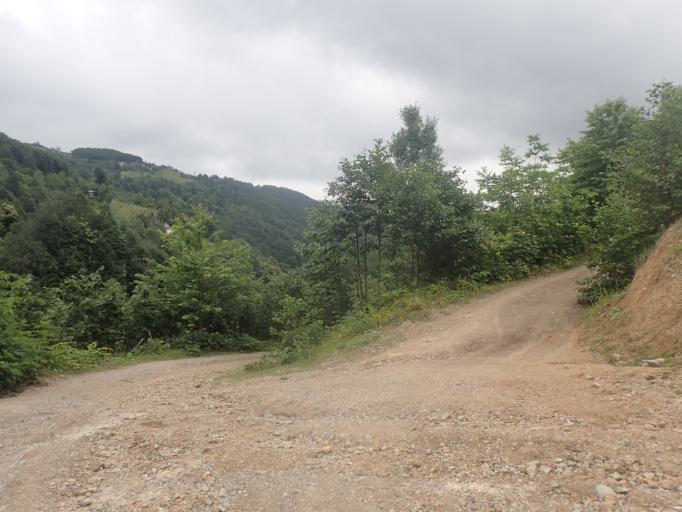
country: TR
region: Ordu
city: Akkus
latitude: 40.8638
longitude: 37.0063
